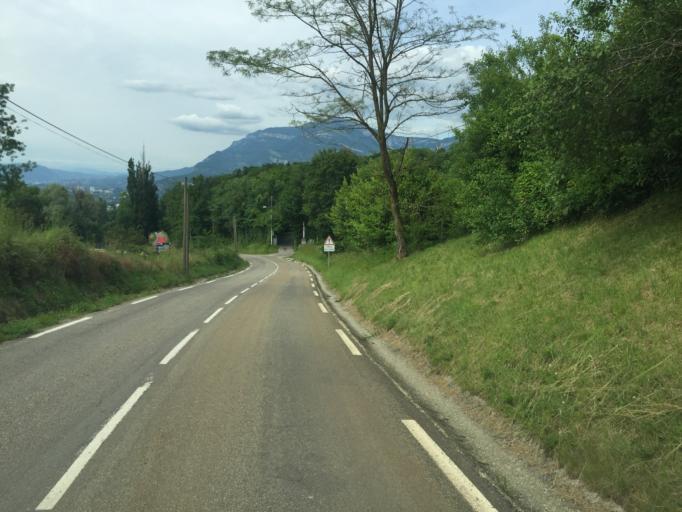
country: FR
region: Rhone-Alpes
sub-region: Departement de la Savoie
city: Jacob-Bellecombette
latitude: 45.5340
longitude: 5.9154
